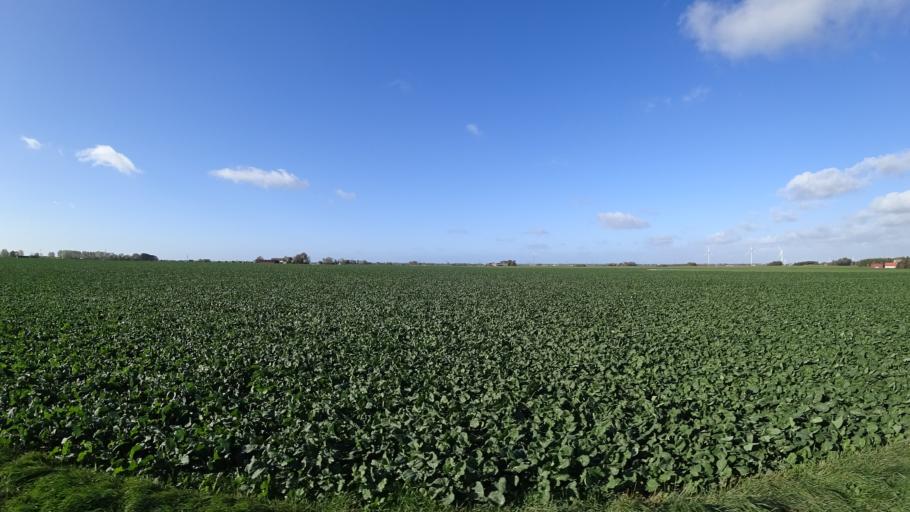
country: SE
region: Skane
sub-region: Staffanstorps Kommun
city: Hjaerup
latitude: 55.6835
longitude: 13.1467
